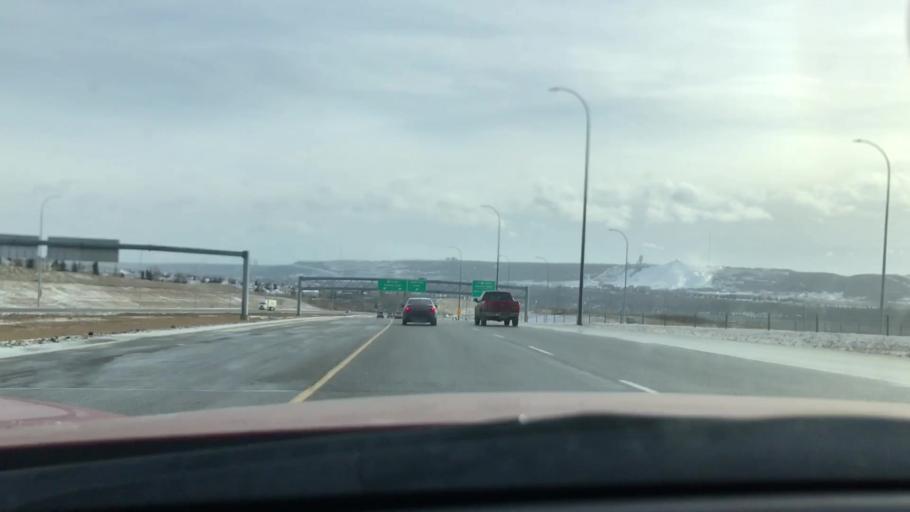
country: CA
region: Alberta
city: Calgary
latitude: 51.1147
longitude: -114.2284
